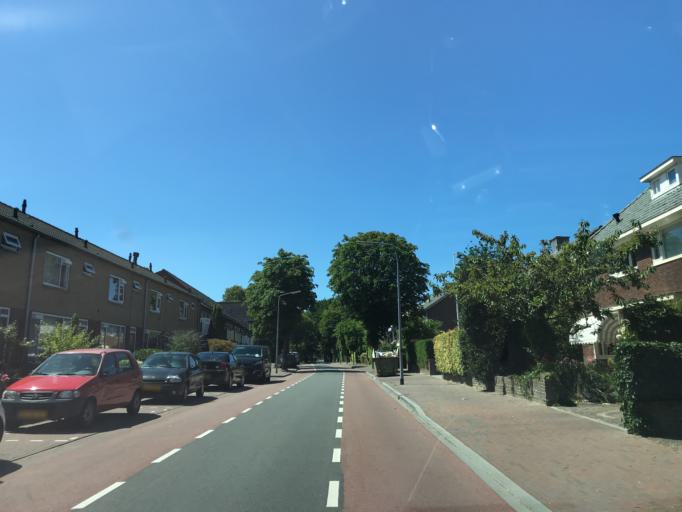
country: NL
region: North Holland
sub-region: Gemeente Huizen
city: Huizen
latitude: 52.3023
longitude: 5.2314
